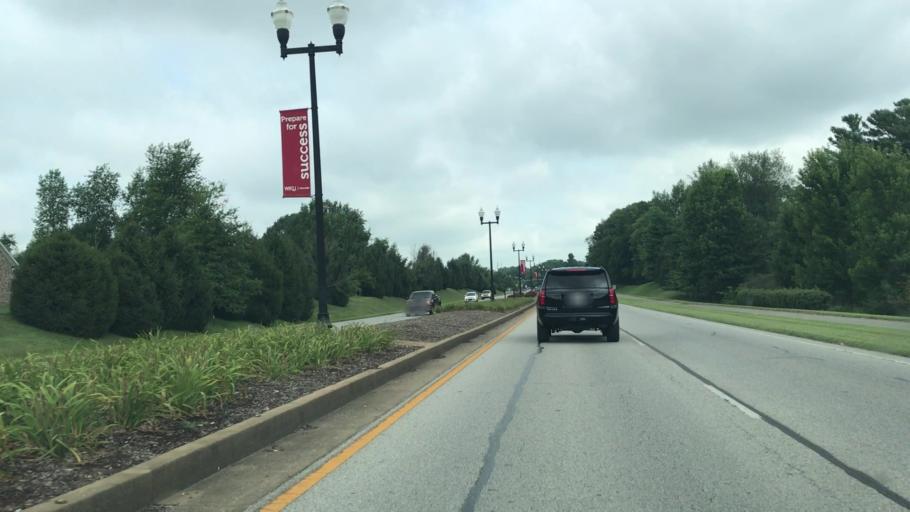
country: US
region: Kentucky
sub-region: Warren County
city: Bowling Green
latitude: 36.9851
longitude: -86.3999
